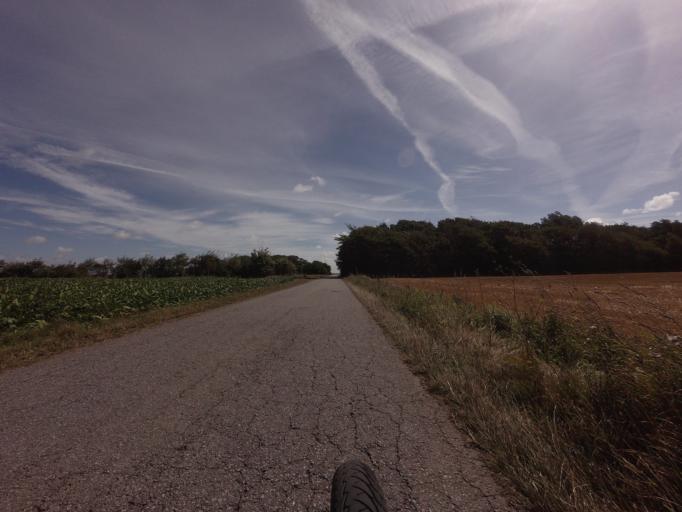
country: DK
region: North Denmark
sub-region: Jammerbugt Kommune
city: Pandrup
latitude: 57.3429
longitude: 9.7816
